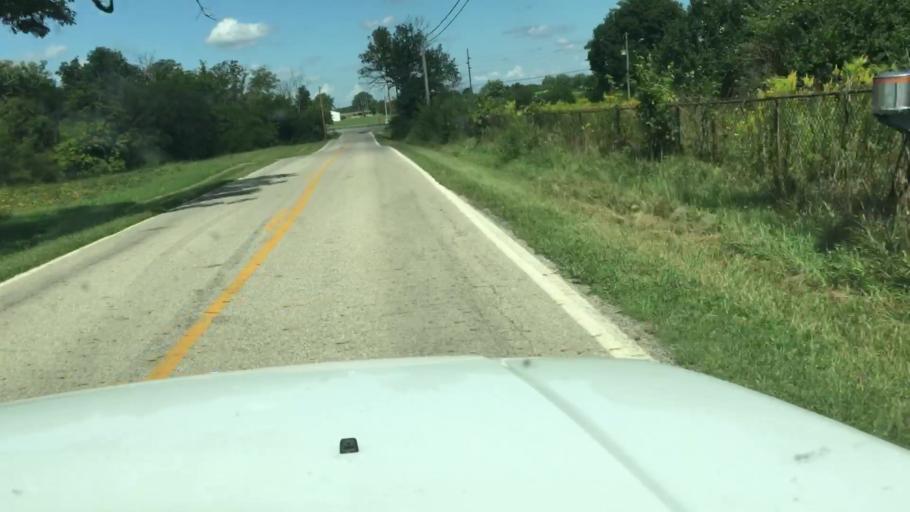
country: US
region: Ohio
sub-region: Madison County
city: Mount Sterling
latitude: 39.7098
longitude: -83.2441
